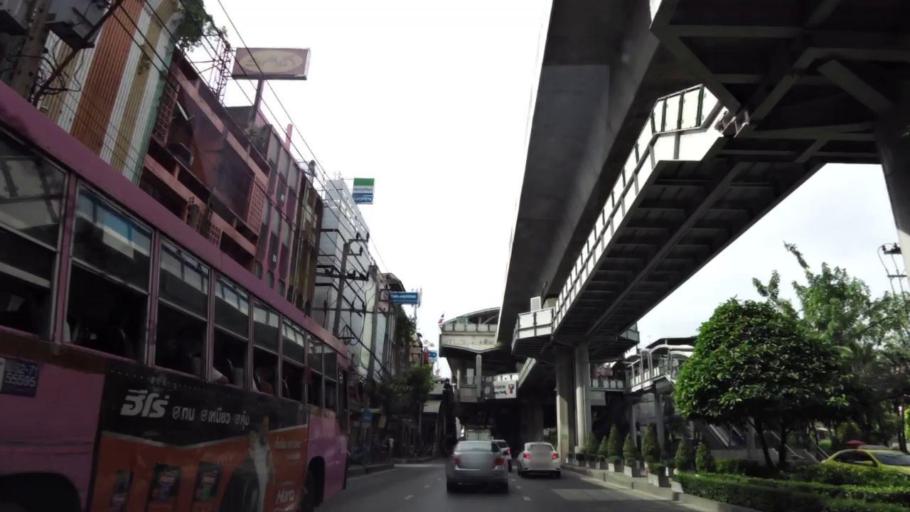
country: TH
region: Bangkok
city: Phra Khanong
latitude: 13.6980
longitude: 100.6049
